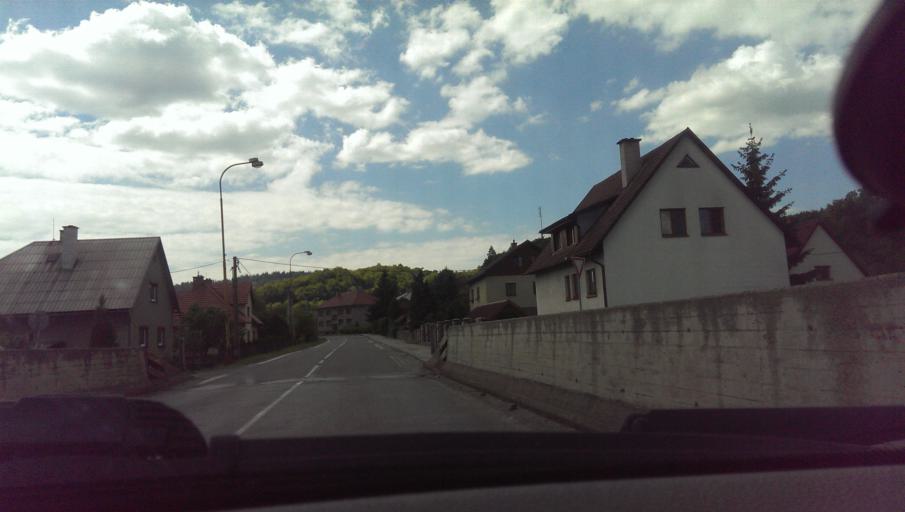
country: CZ
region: Zlin
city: Valasska Polanka
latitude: 49.2686
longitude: 17.9966
